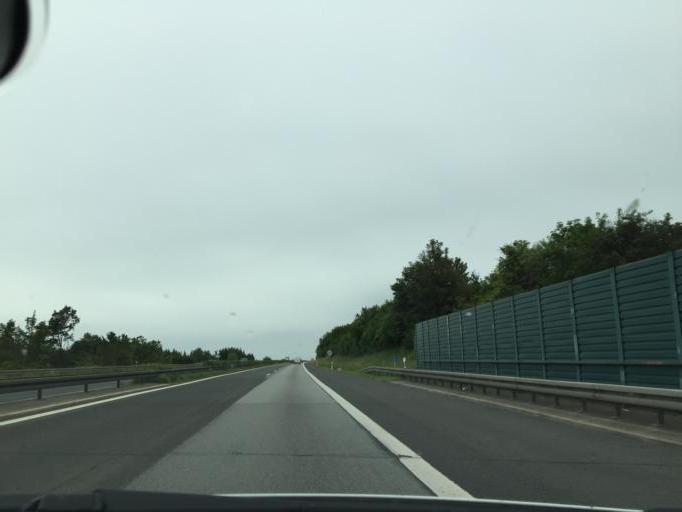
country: DE
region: Bavaria
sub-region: Regierungsbezirk Unterfranken
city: Gochsheim
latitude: 50.0306
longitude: 10.2847
